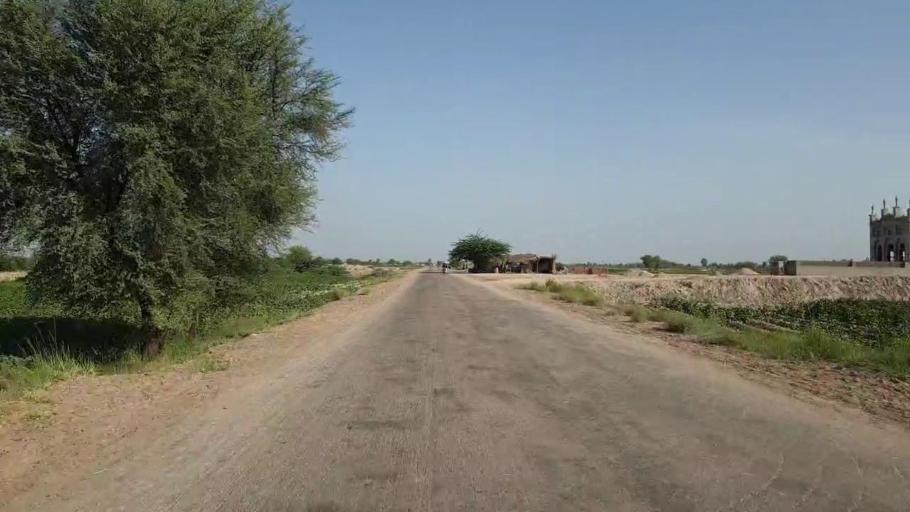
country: PK
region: Sindh
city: Nawabshah
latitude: 26.1418
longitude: 68.4515
